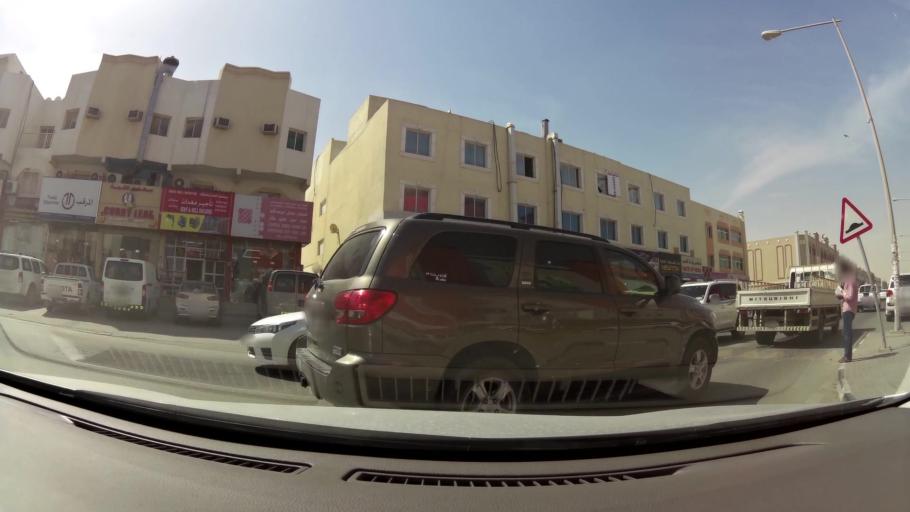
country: QA
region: Baladiyat ar Rayyan
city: Ar Rayyan
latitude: 25.2737
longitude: 51.4078
